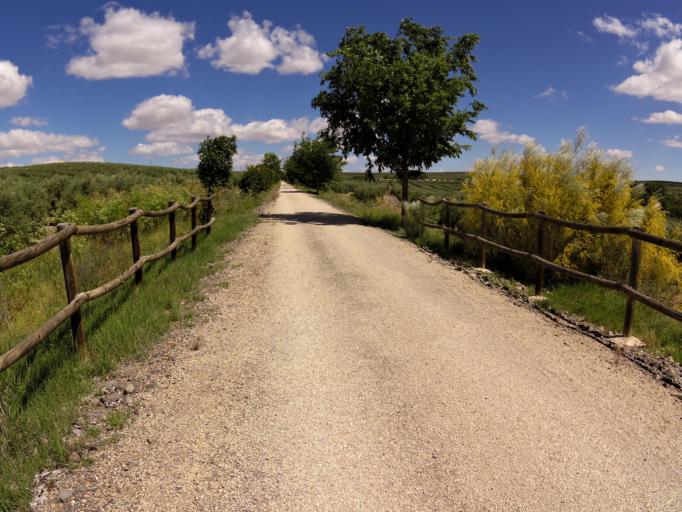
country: ES
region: Andalusia
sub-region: Provincia de Jaen
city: Alcaudete
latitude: 37.6547
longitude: -4.0619
